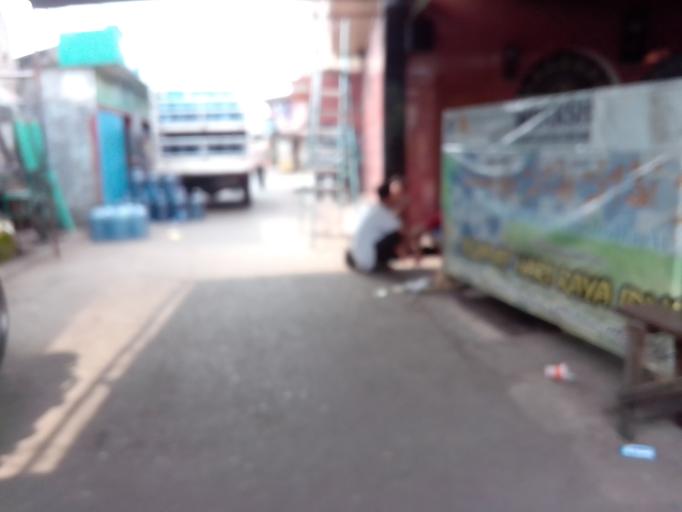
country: ID
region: Jakarta Raya
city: Jakarta
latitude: -6.2030
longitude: 106.8025
